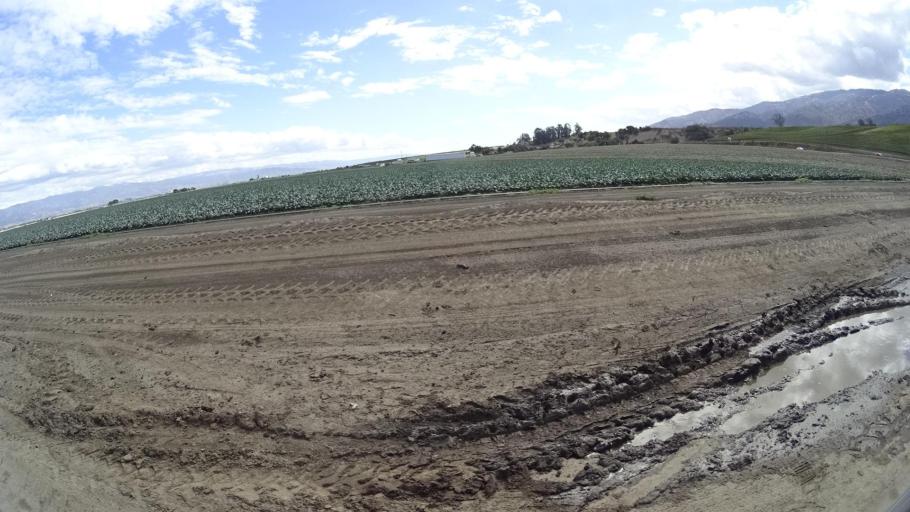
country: US
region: California
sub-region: Monterey County
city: Salinas
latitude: 36.5973
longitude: -121.6194
